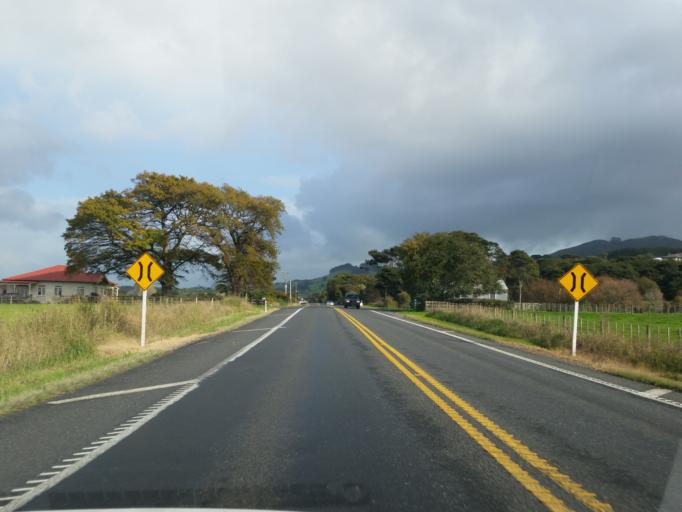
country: NZ
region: Auckland
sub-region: Auckland
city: Pukekohe East
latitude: -37.2153
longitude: 175.0633
